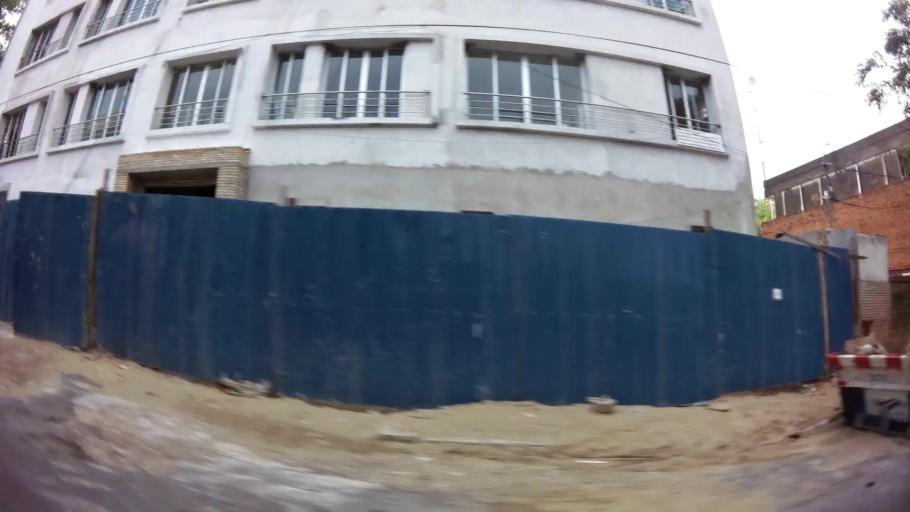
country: PY
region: Asuncion
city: Asuncion
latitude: -25.2887
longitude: -57.6134
